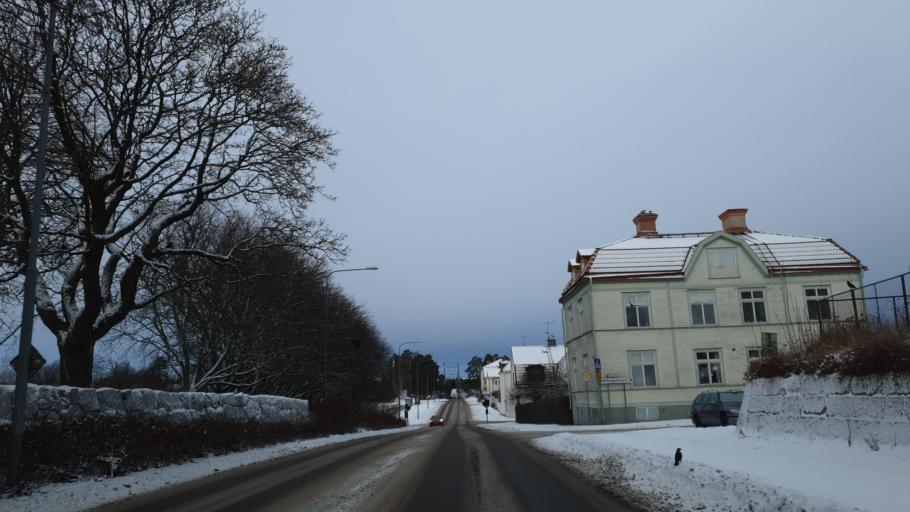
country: SE
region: Gaevleborg
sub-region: Soderhamns Kommun
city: Soderhamn
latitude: 61.3044
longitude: 17.0504
